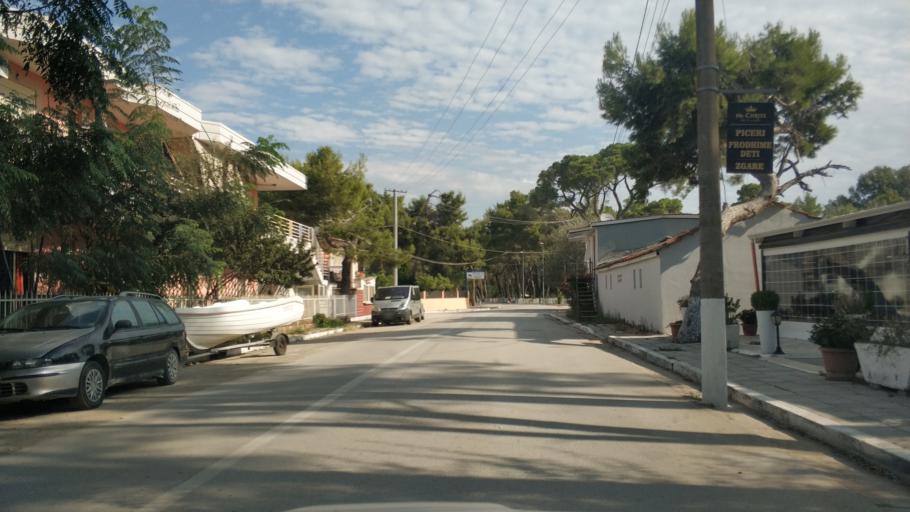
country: AL
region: Fier
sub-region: Rrethi i Lushnjes
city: Divjake
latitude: 40.9716
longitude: 19.4798
